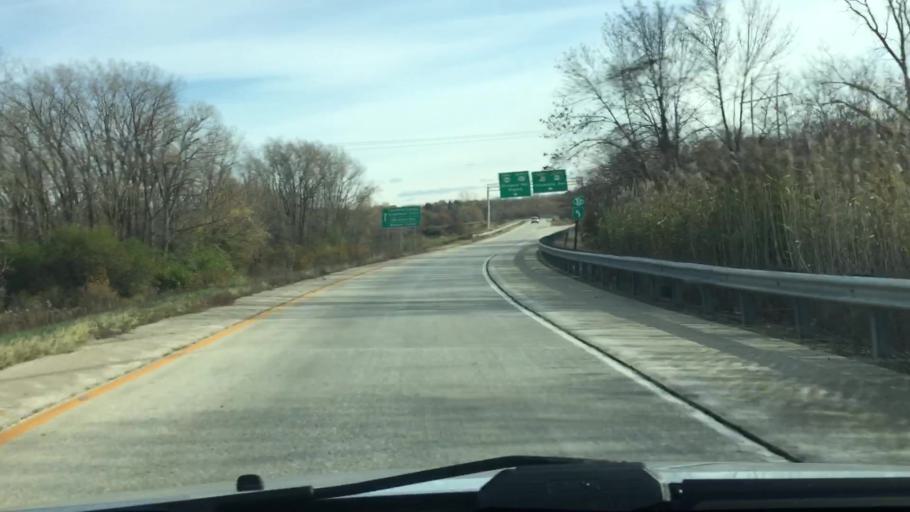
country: US
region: Wisconsin
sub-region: Brown County
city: Green Bay
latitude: 44.5190
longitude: -87.9623
